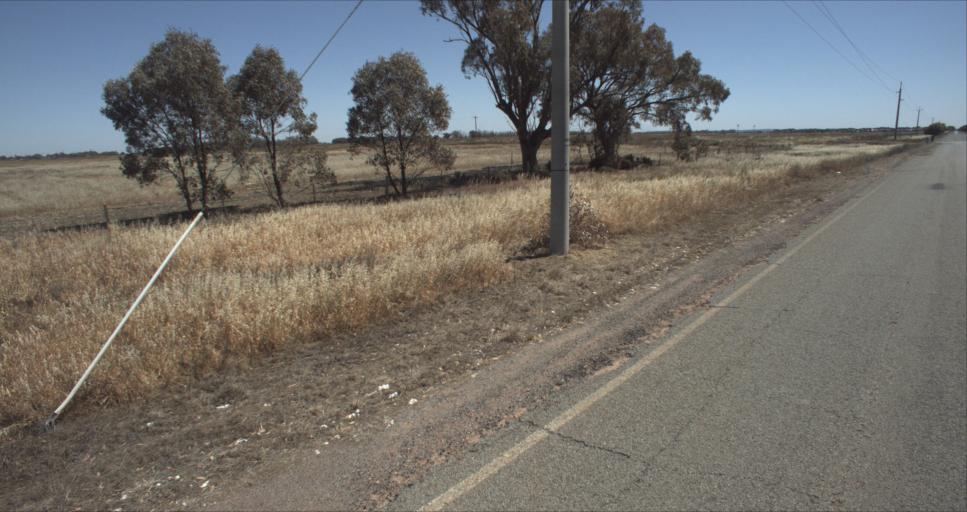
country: AU
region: New South Wales
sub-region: Leeton
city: Leeton
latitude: -34.4943
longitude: 146.2881
